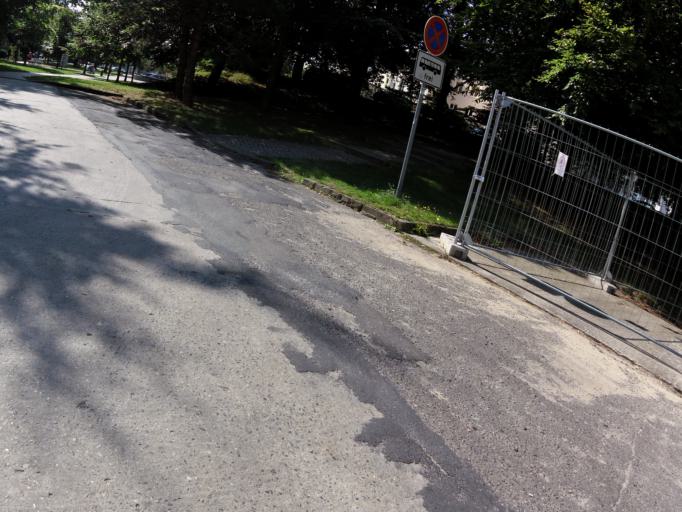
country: DE
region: Mecklenburg-Vorpommern
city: Seebad Heringsdorf
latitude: 53.9552
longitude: 14.1679
